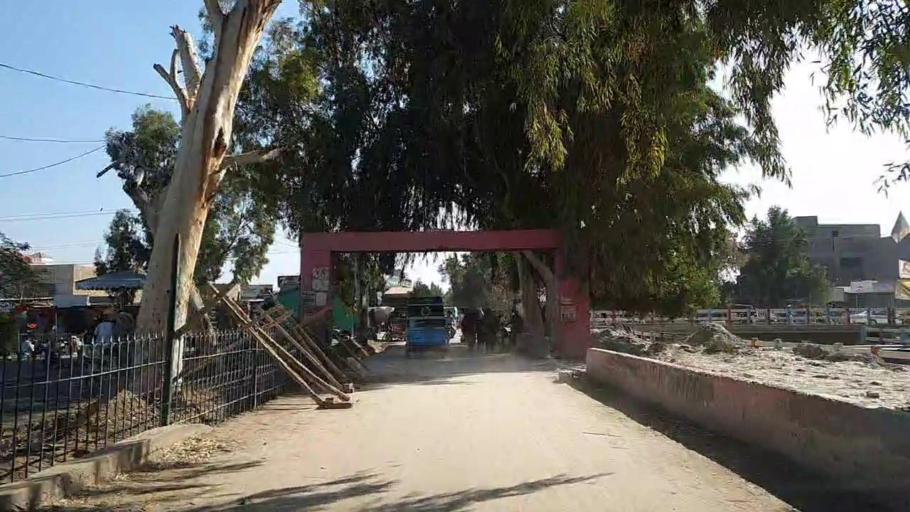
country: PK
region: Sindh
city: Nawabshah
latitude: 26.2530
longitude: 68.4194
